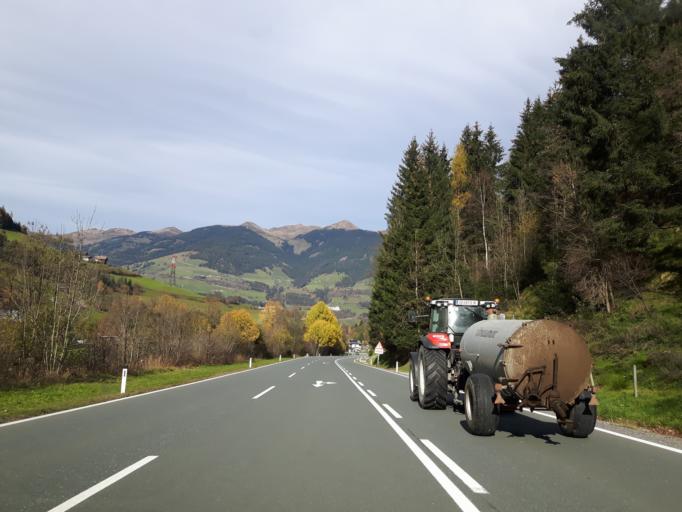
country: AT
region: Salzburg
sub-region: Politischer Bezirk Zell am See
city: Mittersill
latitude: 47.2623
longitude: 12.4845
